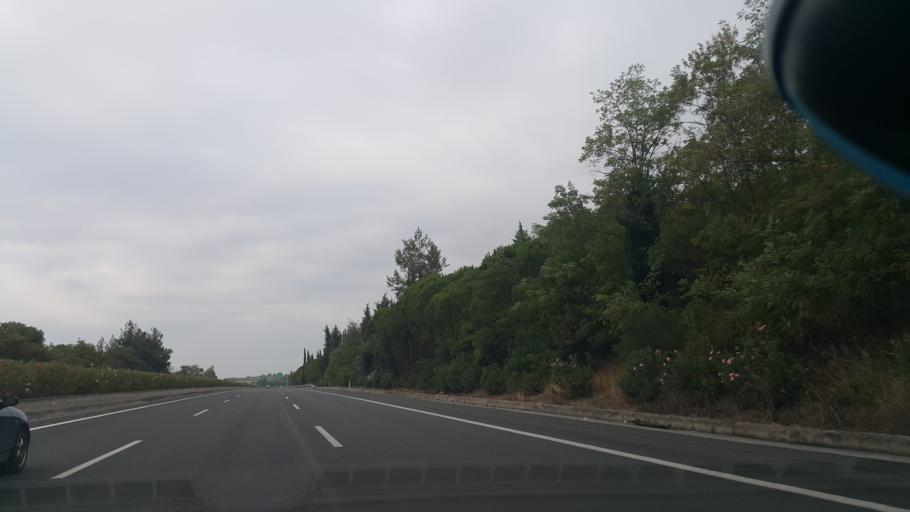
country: GR
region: Central Macedonia
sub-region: Nomos Pierias
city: Makrygialos
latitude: 40.4362
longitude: 22.5859
